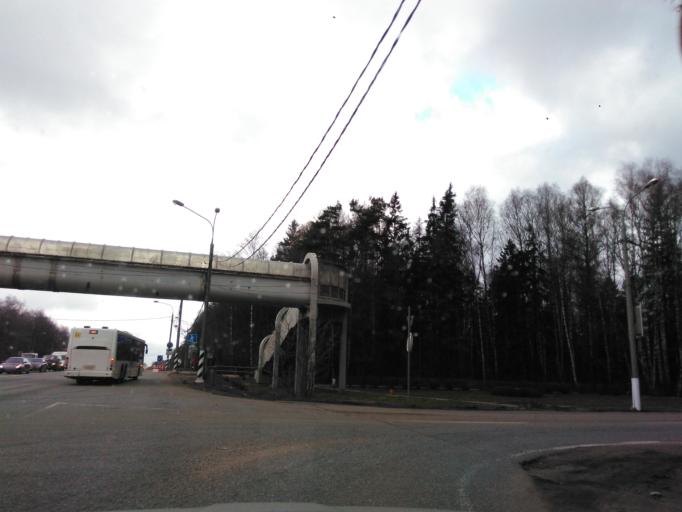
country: RU
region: Moskovskaya
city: Mendeleyevo
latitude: 56.0097
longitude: 37.2196
